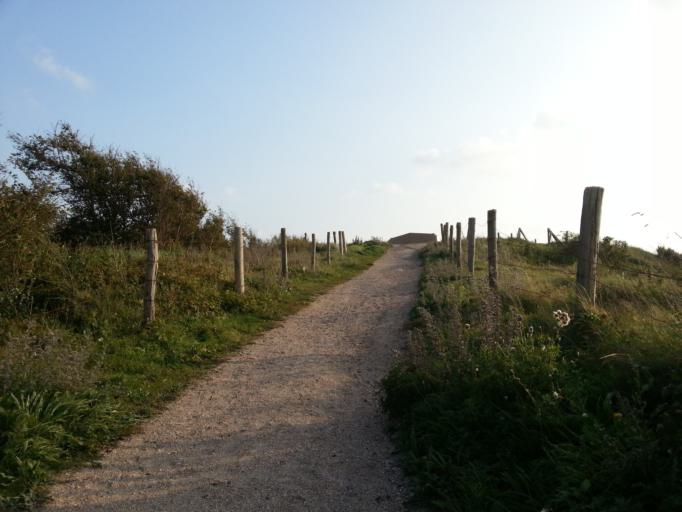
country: NL
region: South Holland
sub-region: Gemeente Westland
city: Poeldijk
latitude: 52.0625
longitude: 4.2181
